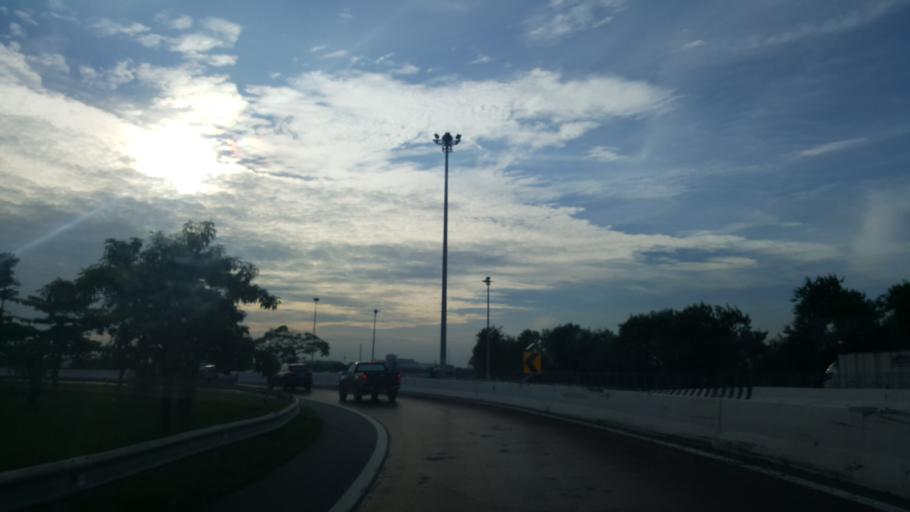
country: TH
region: Chachoengsao
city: Bang Pakong
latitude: 13.6017
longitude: 100.9536
